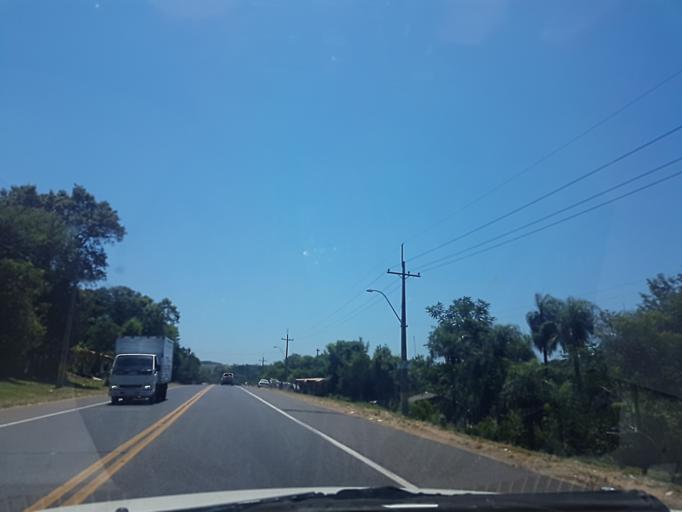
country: PY
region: Cordillera
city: Caacupe
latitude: -25.3909
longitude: -57.0743
